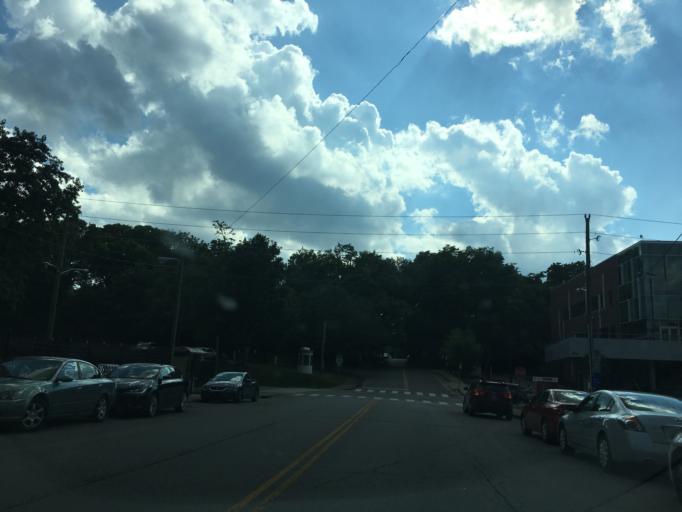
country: US
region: Tennessee
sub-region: Davidson County
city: Nashville
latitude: 36.1659
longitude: -86.8083
